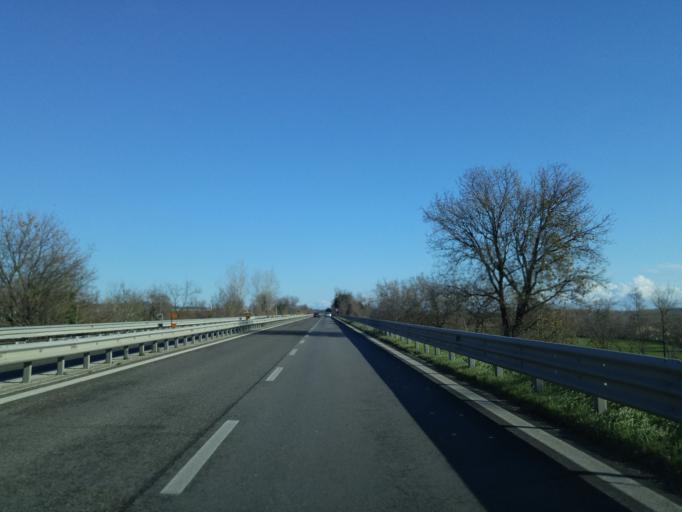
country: IT
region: The Marches
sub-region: Provincia di Pesaro e Urbino
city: Calcinelli
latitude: 43.7543
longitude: 12.9299
